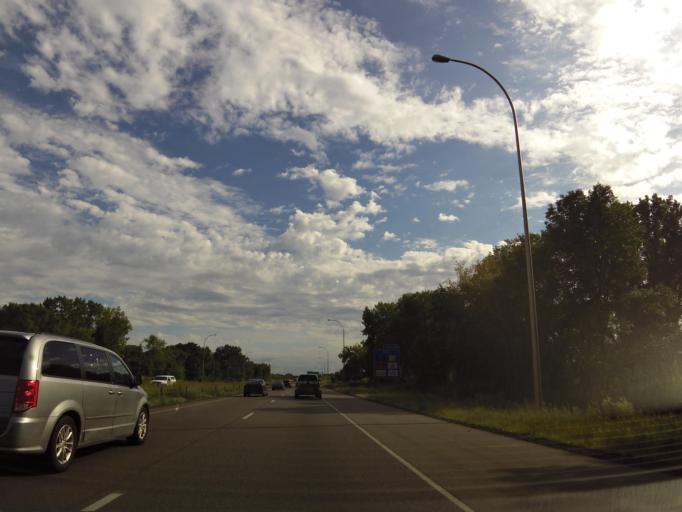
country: US
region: Minnesota
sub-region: Hennepin County
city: New Hope
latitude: 45.0655
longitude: -93.4010
